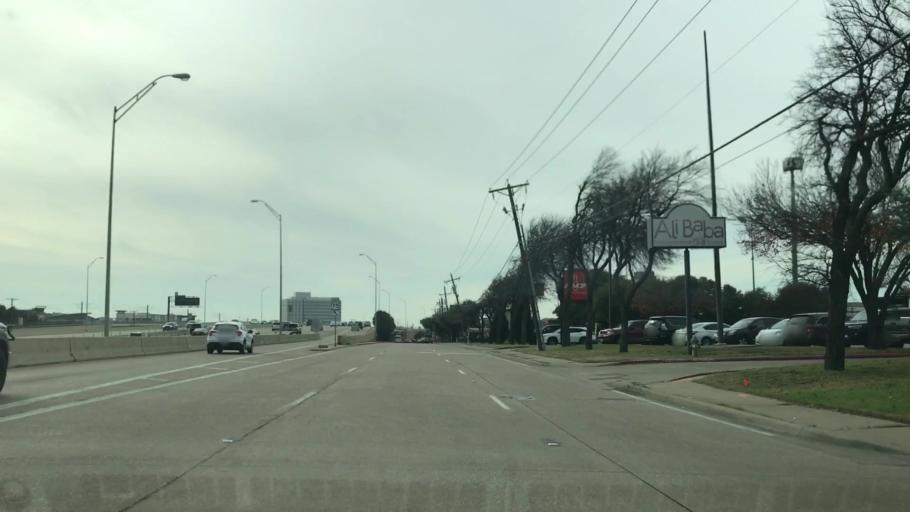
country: US
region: Texas
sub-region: Dallas County
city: Richardson
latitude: 32.9789
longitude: -96.7149
